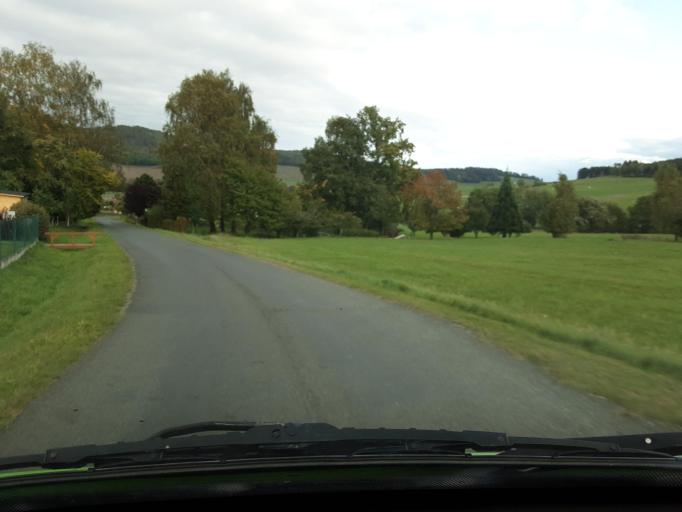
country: CZ
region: Plzensky
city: Janovice nad Uhlavou
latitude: 49.3860
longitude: 13.1426
